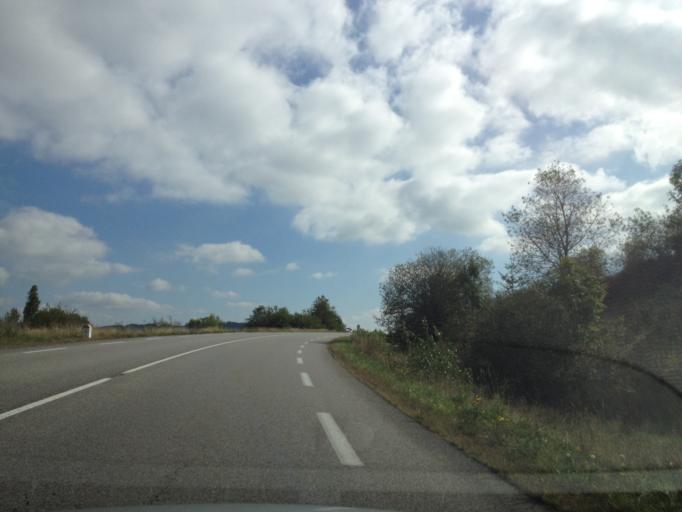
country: FR
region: Rhone-Alpes
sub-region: Departement de la Loire
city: Lentigny
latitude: 45.9476
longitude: 3.9817
